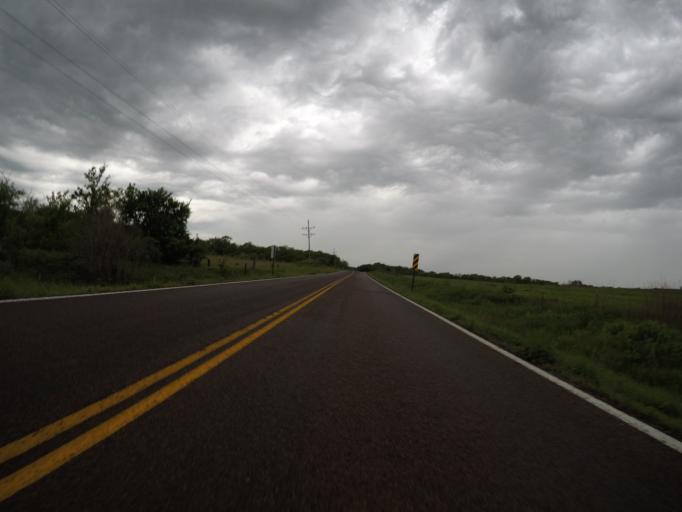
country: US
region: Kansas
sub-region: Shawnee County
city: Rossville
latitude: 38.9574
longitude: -96.0633
